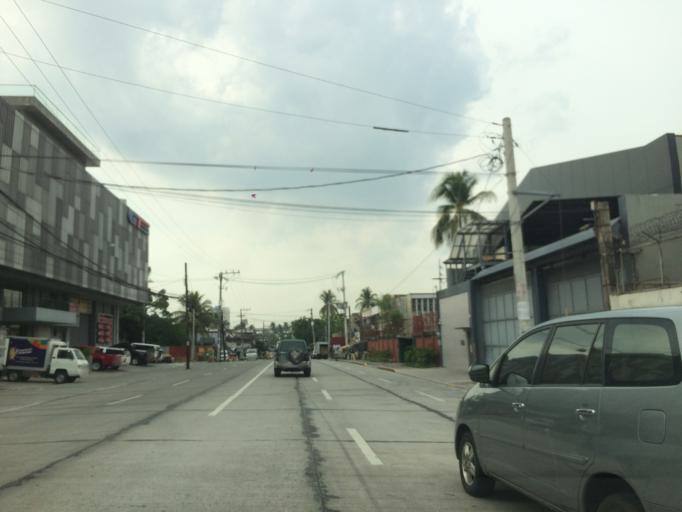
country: PH
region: Calabarzon
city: Del Monte
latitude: 14.6401
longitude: 121.0053
